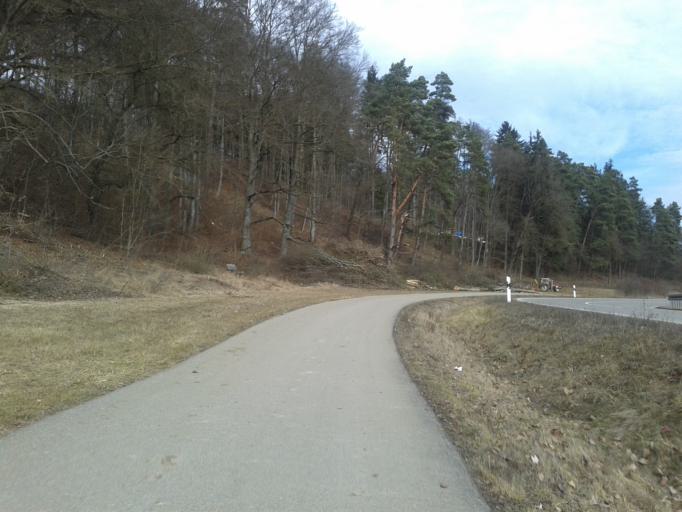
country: DE
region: Baden-Wuerttemberg
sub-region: Tuebingen Region
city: Schelklingen
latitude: 48.3656
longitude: 9.7242
